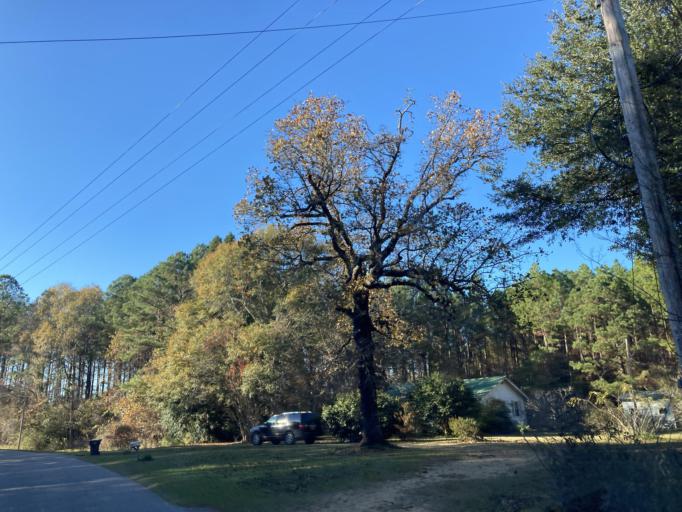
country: US
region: Mississippi
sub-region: Lamar County
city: Sumrall
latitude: 31.3660
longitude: -89.5645
